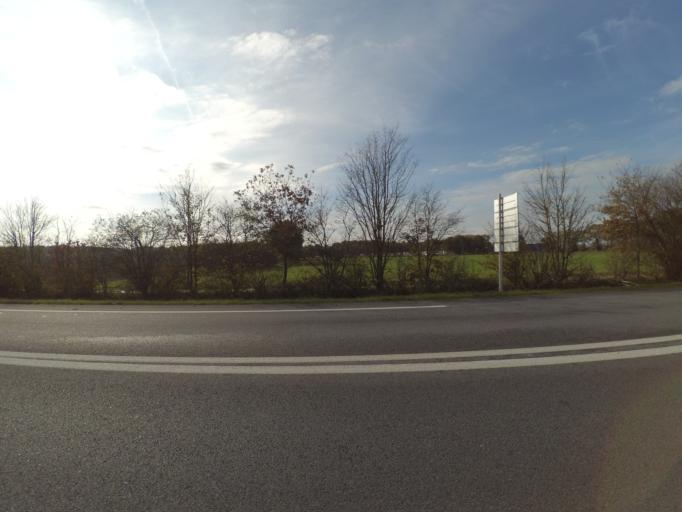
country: FR
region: Pays de la Loire
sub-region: Departement de la Vendee
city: Saint-Hilaire-de-Loulay
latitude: 47.0207
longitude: -1.3454
